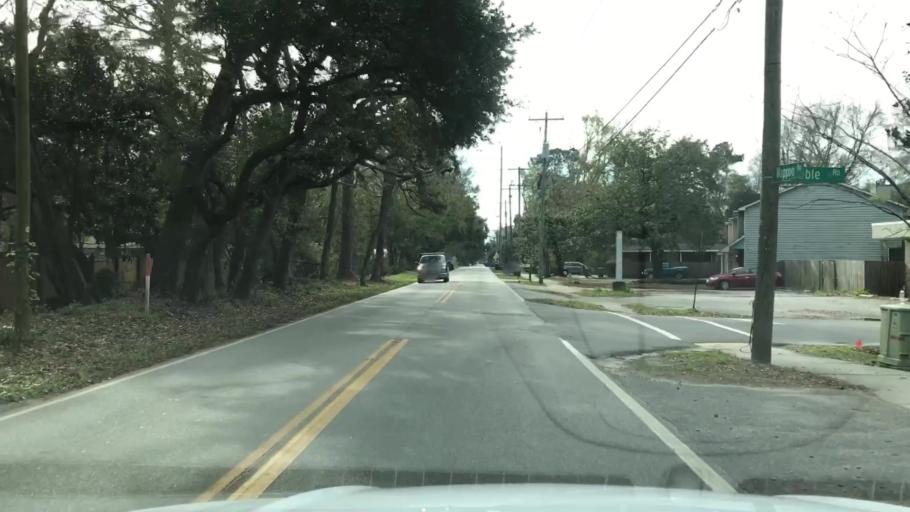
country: US
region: South Carolina
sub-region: Charleston County
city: North Charleston
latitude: 32.7869
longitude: -80.0206
